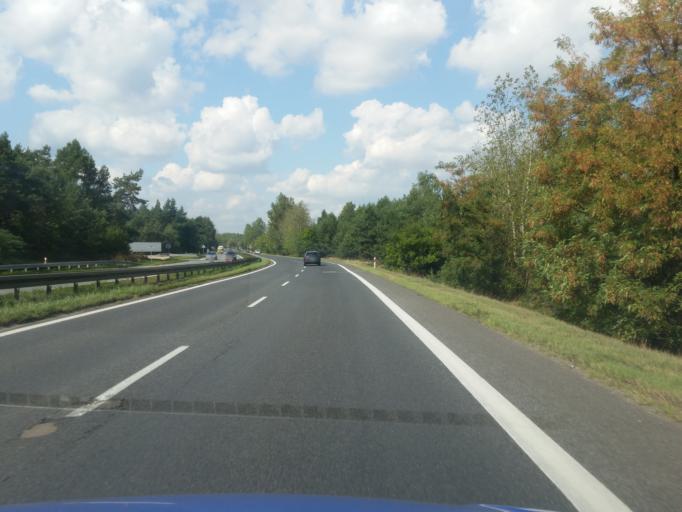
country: PL
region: Silesian Voivodeship
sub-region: Powiat bedzinski
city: Siewierz
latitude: 50.4793
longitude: 19.2260
